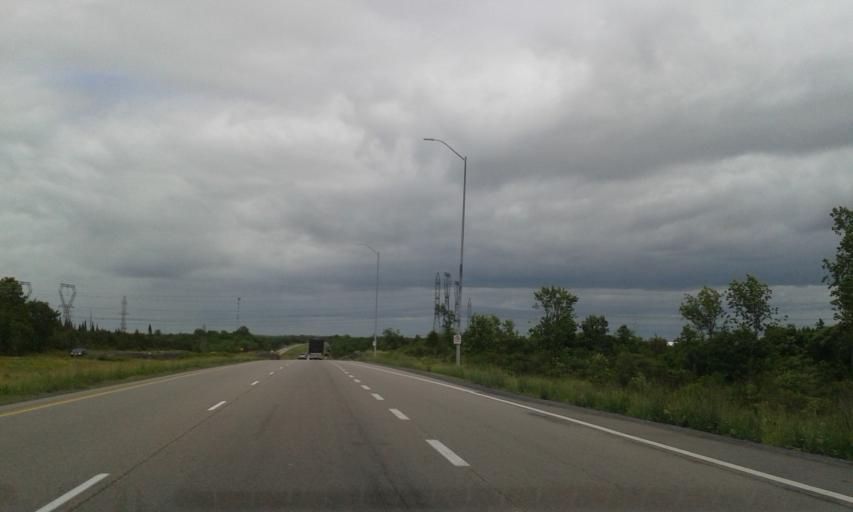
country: CA
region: Ontario
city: Kingston
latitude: 44.2855
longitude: -76.6500
